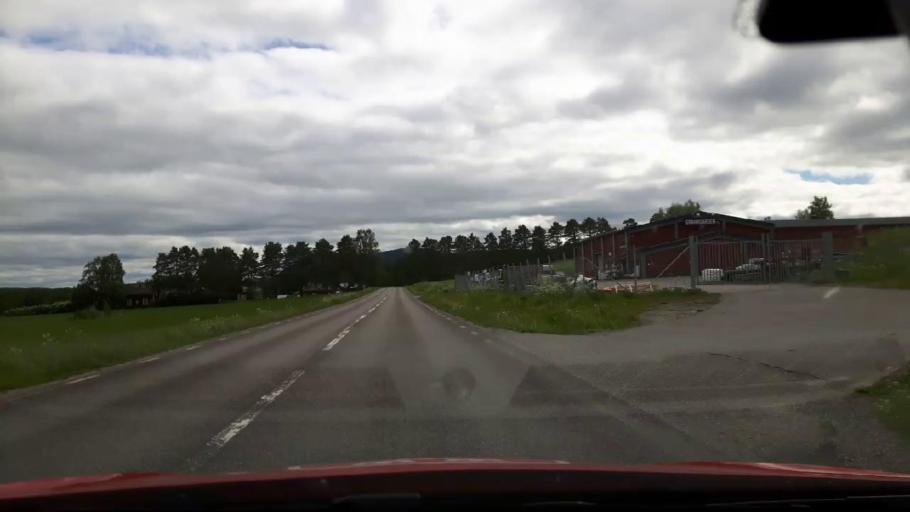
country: SE
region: Jaemtland
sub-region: Ragunda Kommun
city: Hammarstrand
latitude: 63.0983
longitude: 16.3574
